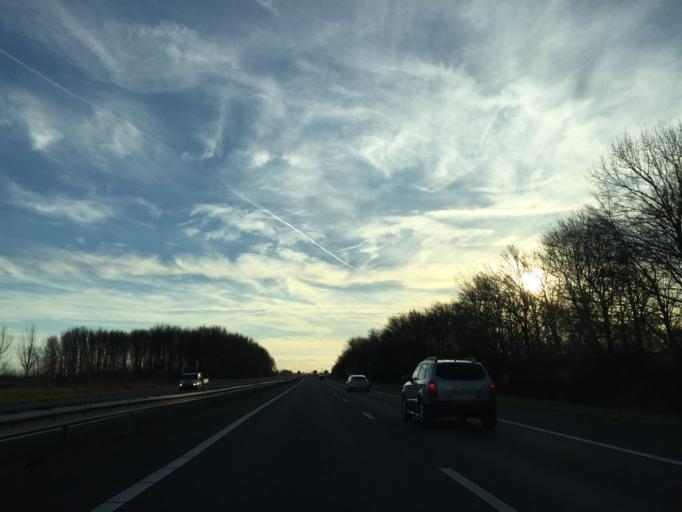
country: NL
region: North Brabant
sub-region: Gemeente Moerdijk
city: Willemstad
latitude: 51.7512
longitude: 4.4155
